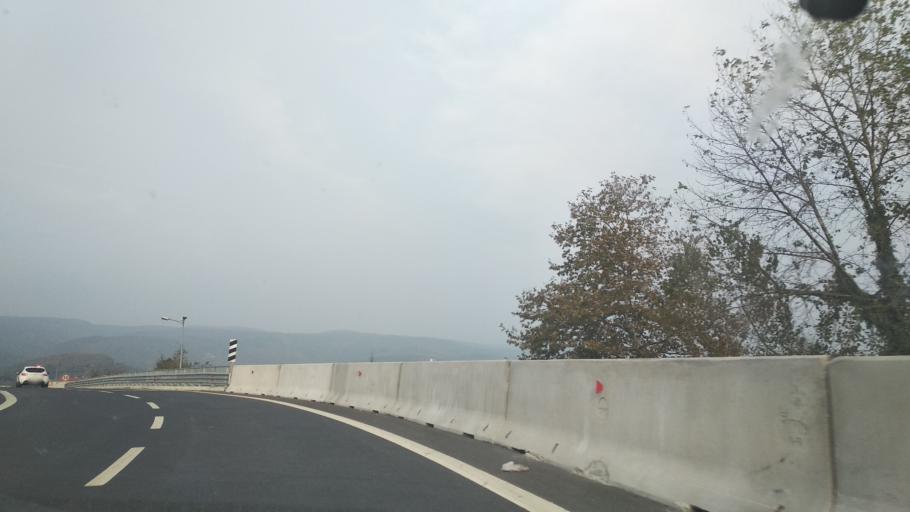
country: TR
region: Duzce
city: Kaynasli
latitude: 40.7815
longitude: 31.2768
